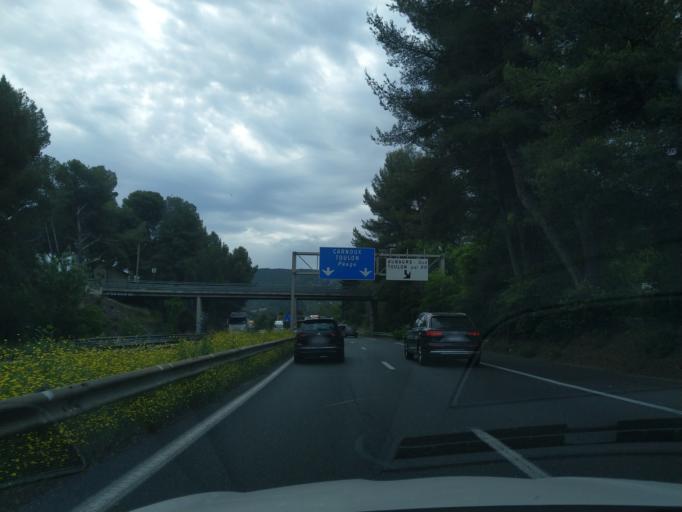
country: FR
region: Provence-Alpes-Cote d'Azur
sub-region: Departement des Bouches-du-Rhone
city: Aubagne
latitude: 43.2847
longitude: 5.5718
